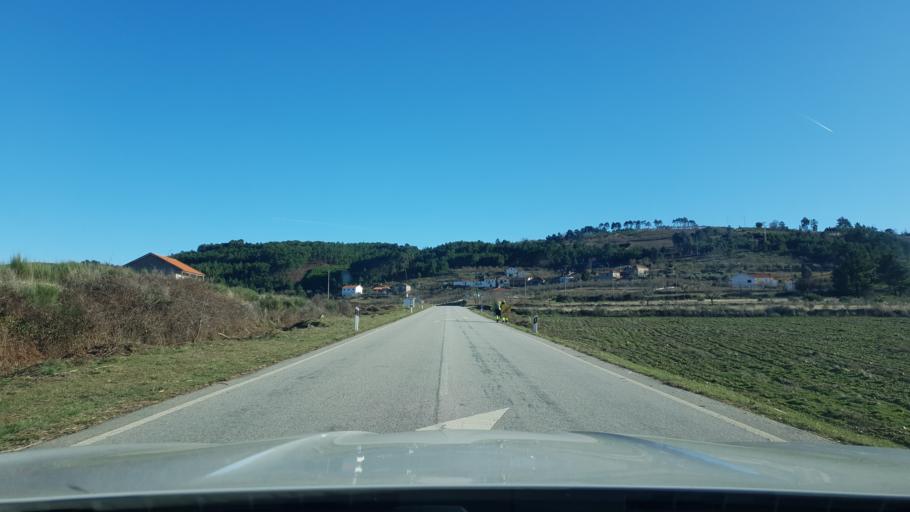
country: PT
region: Braganca
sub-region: Freixo de Espada A Cinta
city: Freixo de Espada a Cinta
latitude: 41.1824
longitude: -6.8229
